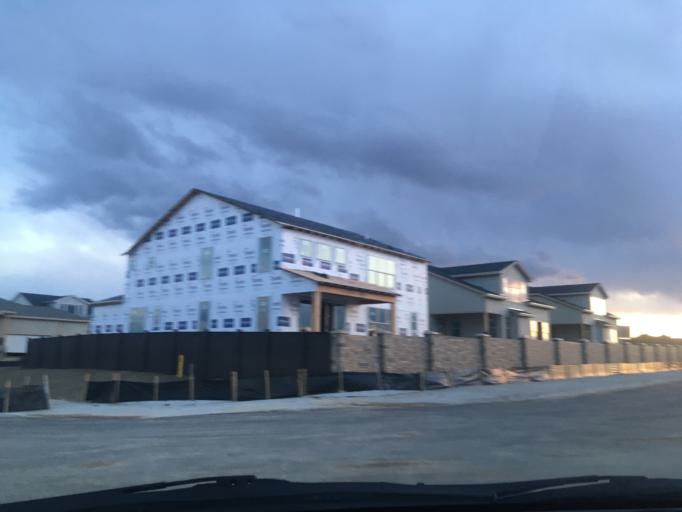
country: US
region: Colorado
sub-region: Adams County
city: Todd Creek
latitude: 39.9575
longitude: -104.9131
